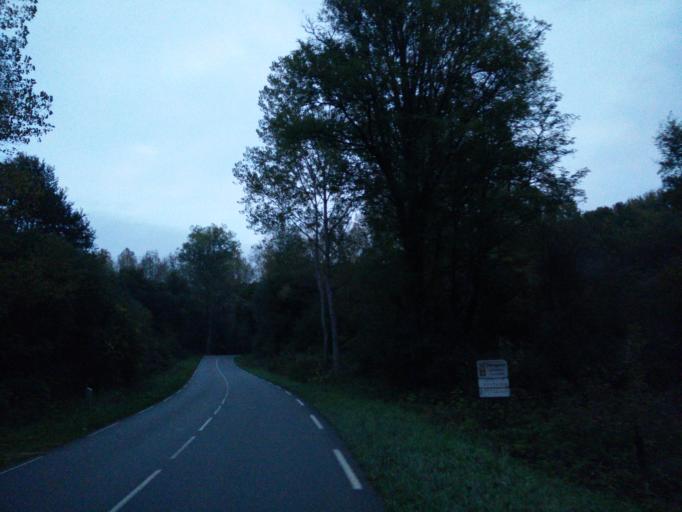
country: FR
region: Aquitaine
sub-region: Departement de la Dordogne
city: Sarlat-la-Caneda
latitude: 44.9060
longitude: 1.1301
